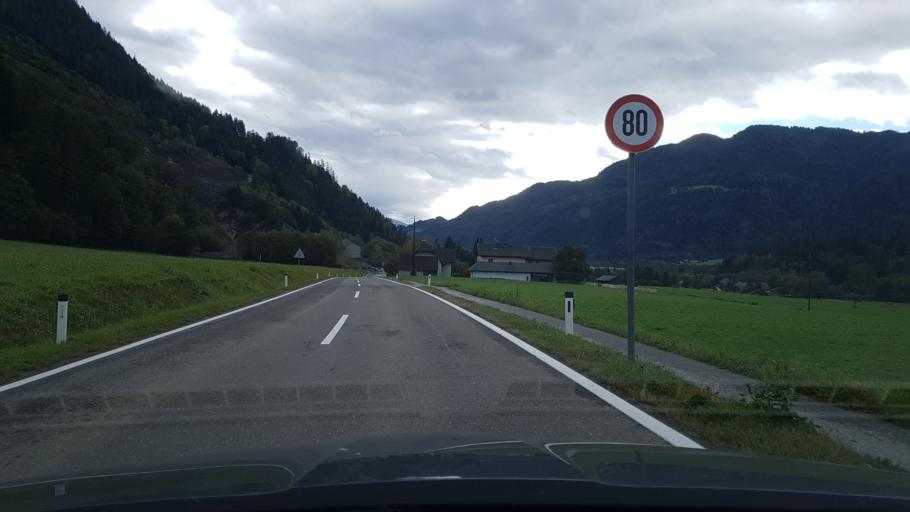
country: AT
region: Styria
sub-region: Politischer Bezirk Murau
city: Oberwolz Stadt
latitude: 47.1489
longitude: 14.2740
